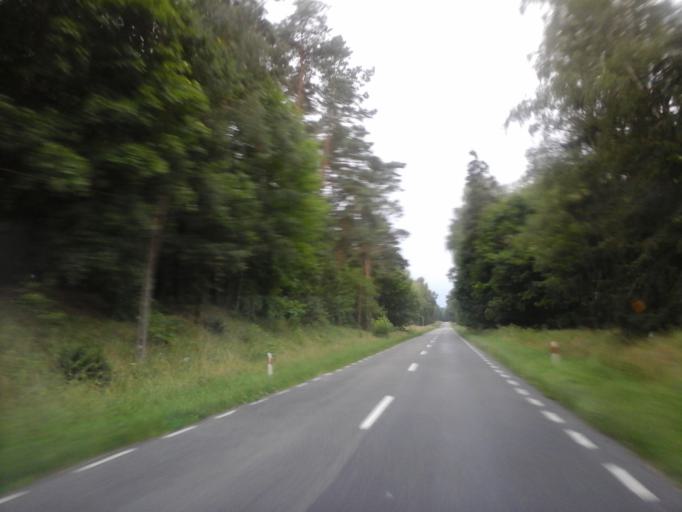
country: PL
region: West Pomeranian Voivodeship
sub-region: Powiat choszczenski
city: Recz
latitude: 53.2443
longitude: 15.5144
